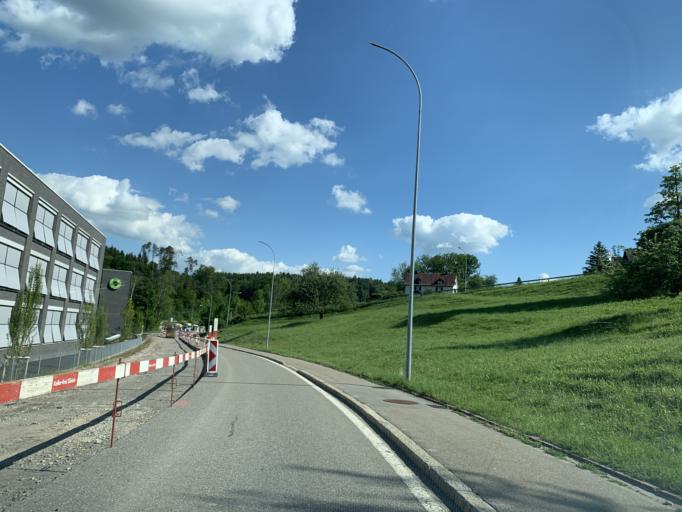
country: CH
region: Zurich
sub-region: Bezirk Pfaeffikon
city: Effretikon / Watt
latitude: 47.4460
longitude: 8.7023
